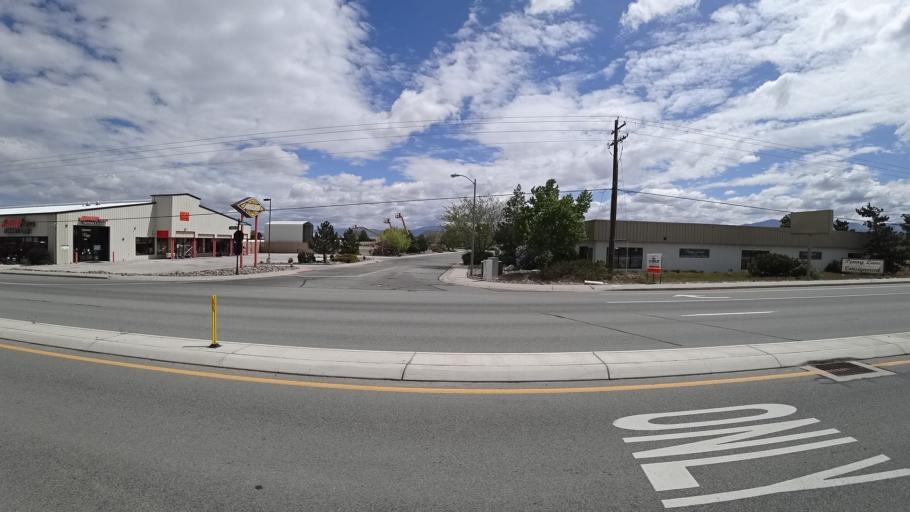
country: US
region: Nevada
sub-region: Douglas County
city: Gardnerville
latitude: 38.9239
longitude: -119.7265
